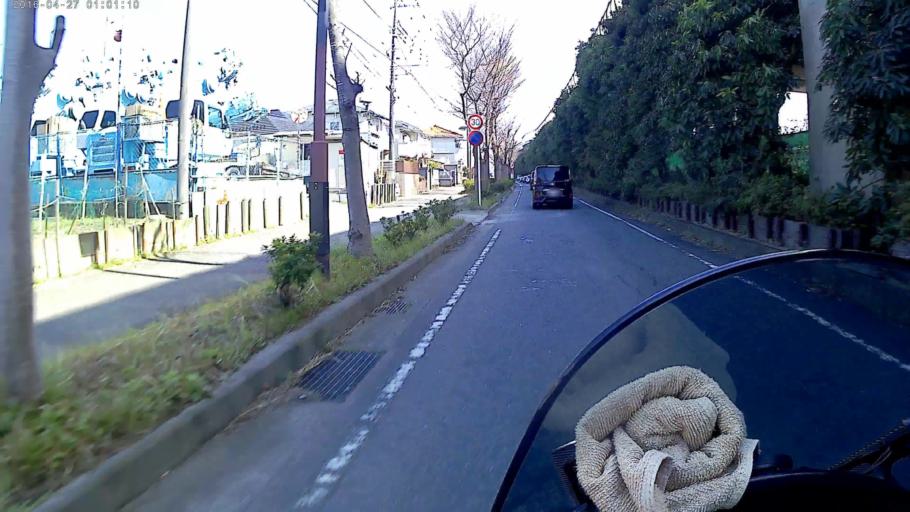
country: JP
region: Kanagawa
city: Chigasaki
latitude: 35.3482
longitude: 139.4230
